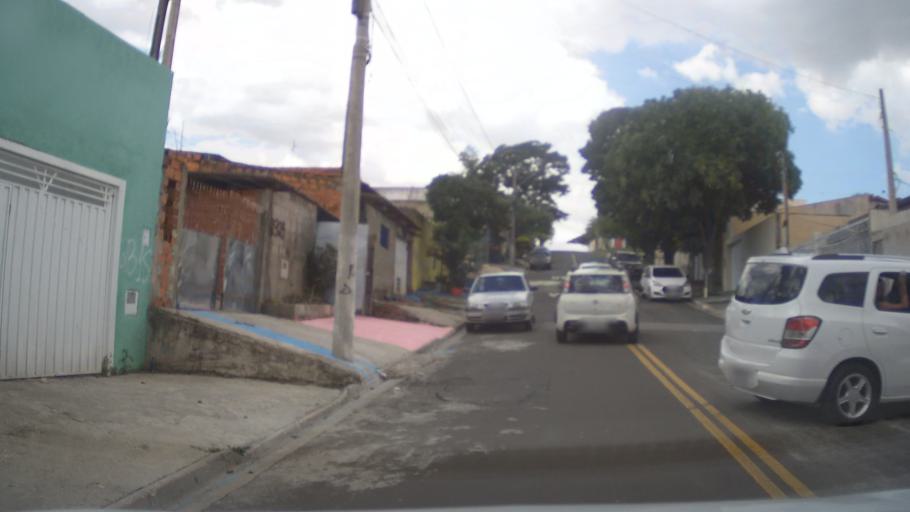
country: BR
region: Sao Paulo
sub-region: Campinas
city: Campinas
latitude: -22.9174
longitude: -47.0205
